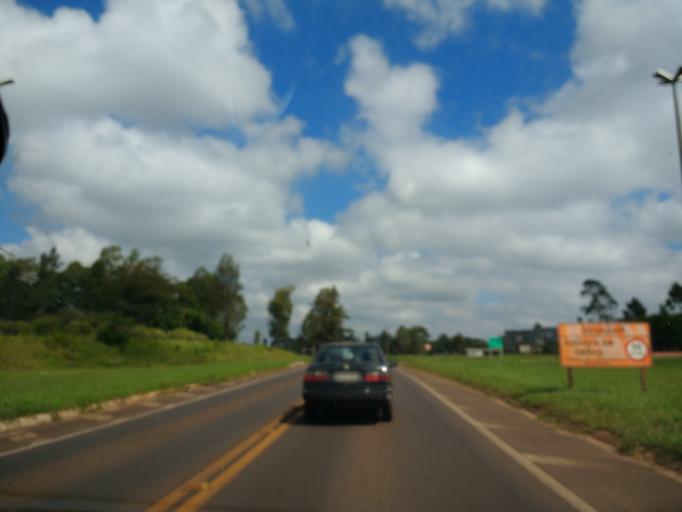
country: BR
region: Parana
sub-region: Cruzeiro Do Oeste
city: Cruzeiro do Oeste
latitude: -23.7949
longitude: -53.0471
